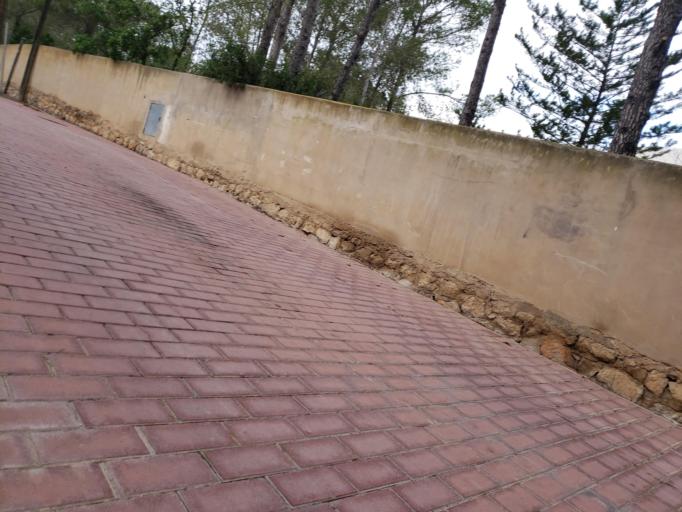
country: ES
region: Balearic Islands
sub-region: Illes Balears
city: Sant Joan de Labritja
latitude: 39.1091
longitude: 1.5141
